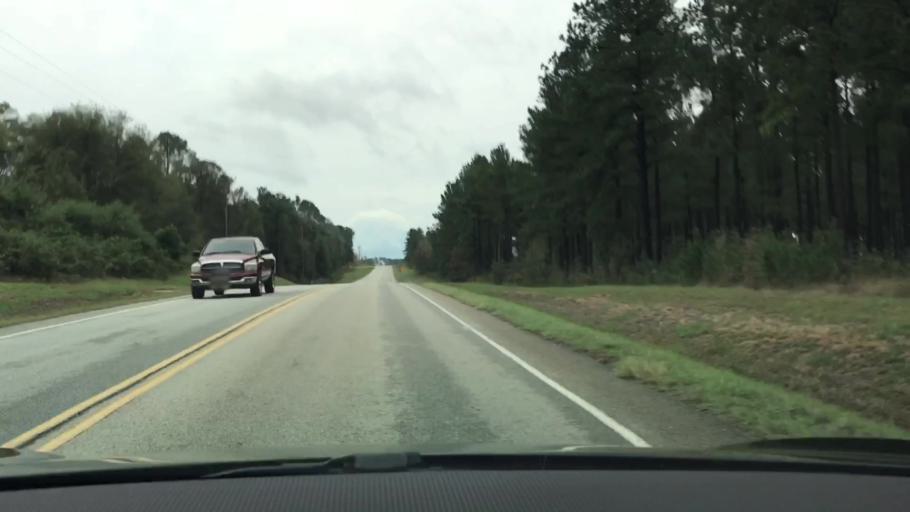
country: US
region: Georgia
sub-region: Jefferson County
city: Louisville
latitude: 33.0883
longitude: -82.4151
